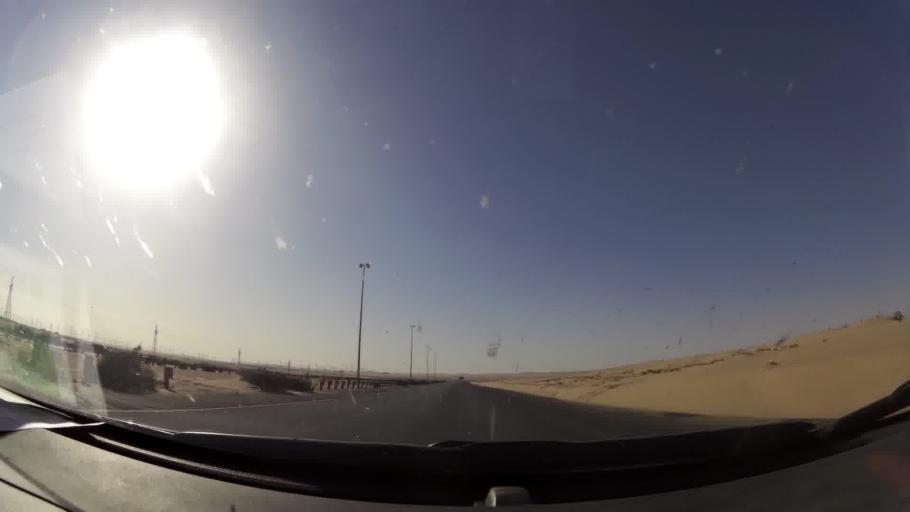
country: KW
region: Al Asimah
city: Kuwait City
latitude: 29.6450
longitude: 47.9516
